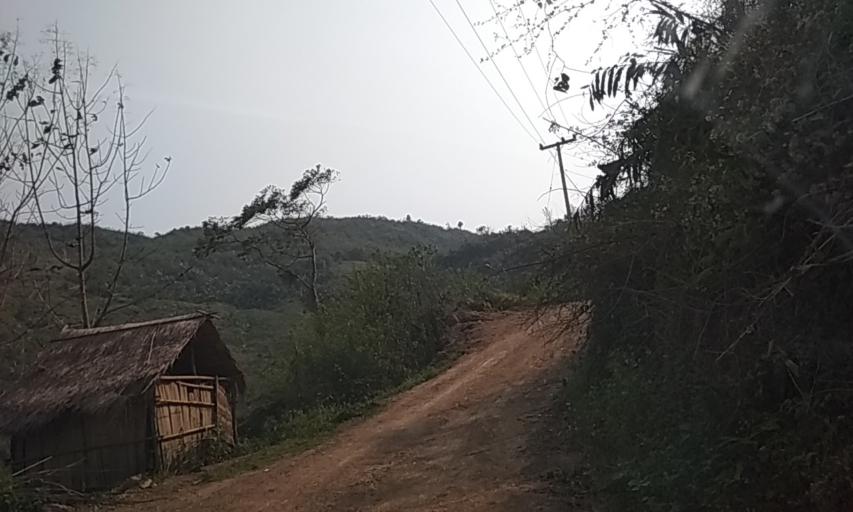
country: LA
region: Louangphabang
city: Louangphabang
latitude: 20.0527
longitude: 101.8564
